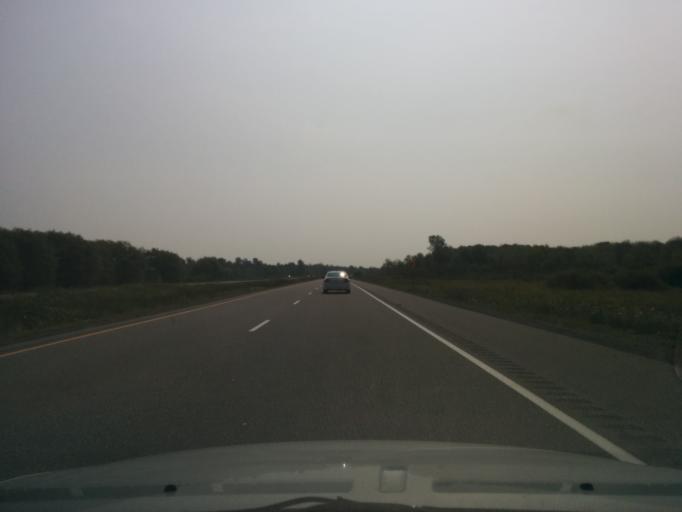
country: CA
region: Ontario
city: Bells Corners
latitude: 45.1091
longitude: -75.6663
